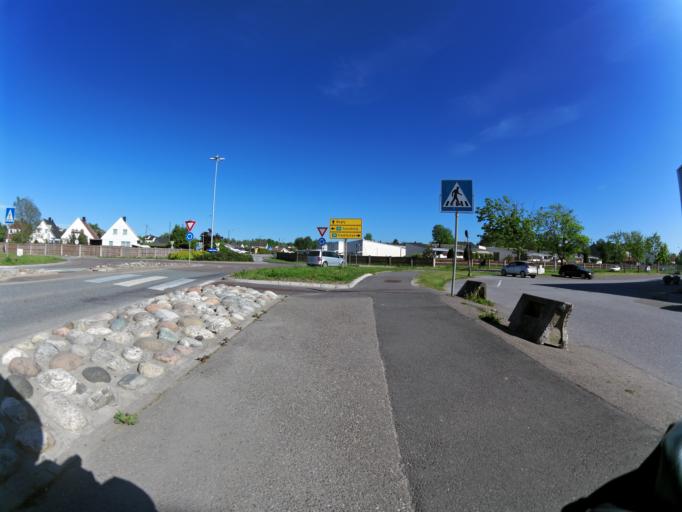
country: NO
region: Ostfold
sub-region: Fredrikstad
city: Fredrikstad
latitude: 59.2272
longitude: 10.9967
